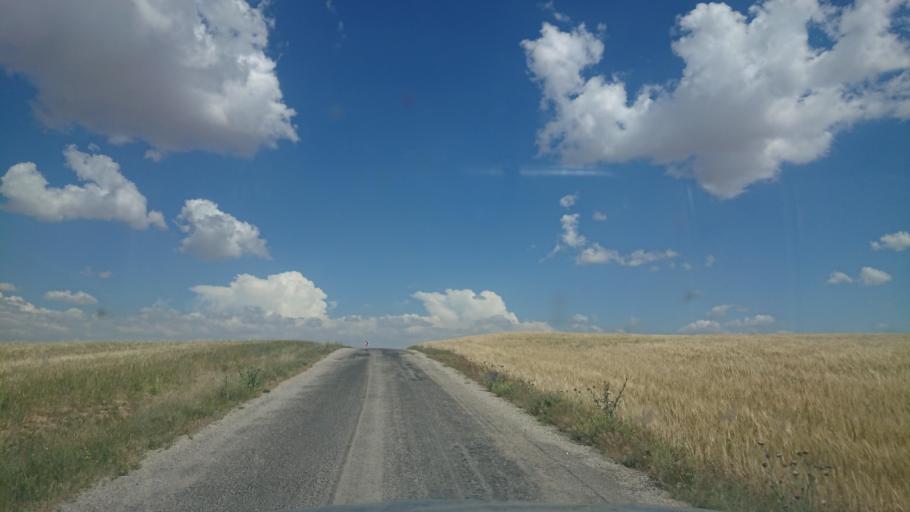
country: TR
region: Aksaray
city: Agacoren
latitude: 38.8066
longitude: 33.8077
